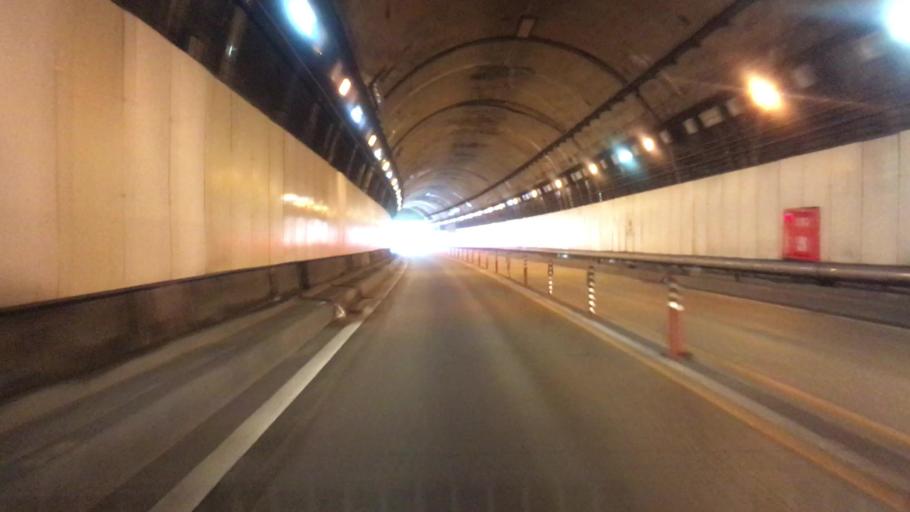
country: JP
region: Kyoto
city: Fukuchiyama
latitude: 35.3027
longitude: 134.9294
